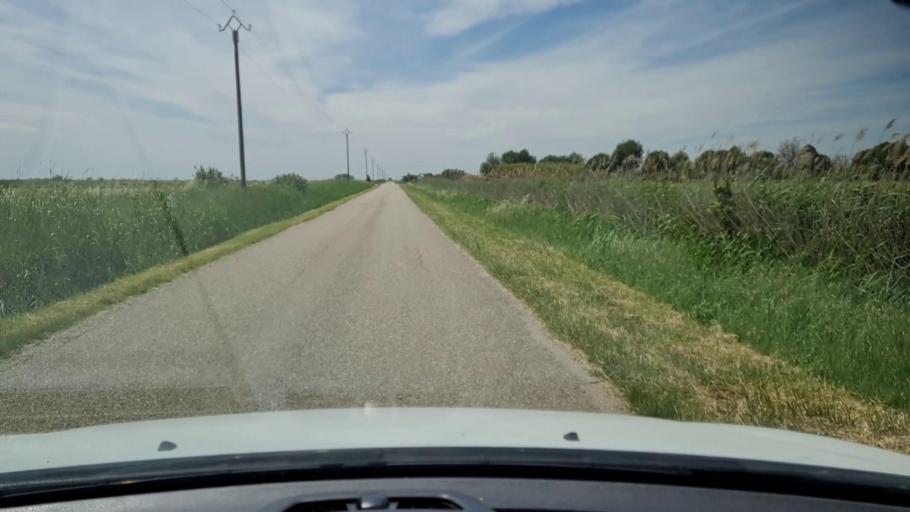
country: FR
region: Languedoc-Roussillon
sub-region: Departement du Gard
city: Saint-Gilles
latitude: 43.6032
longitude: 4.4523
